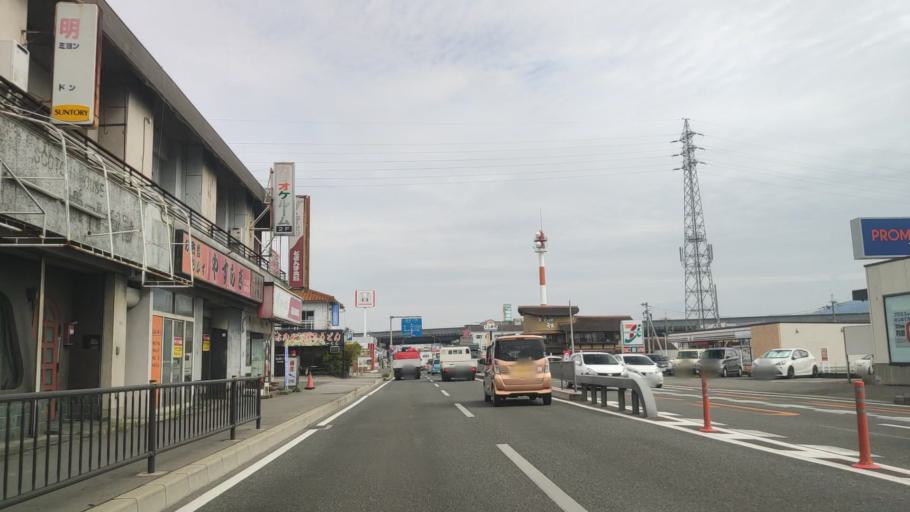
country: JP
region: Osaka
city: Kashihara
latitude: 34.5662
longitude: 135.6053
